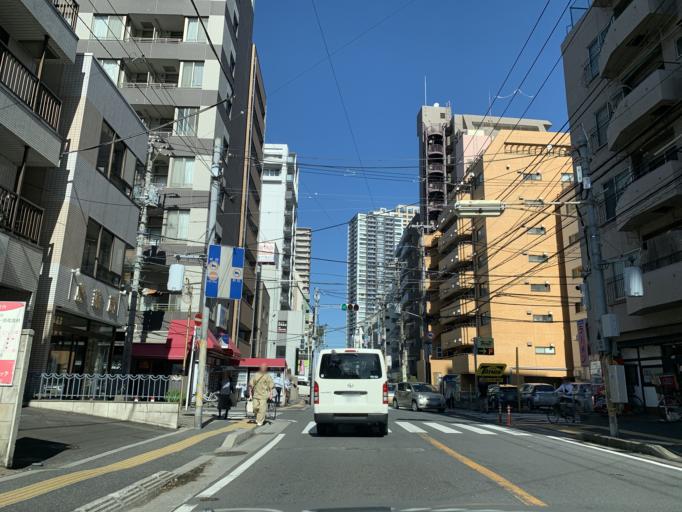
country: JP
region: Tokyo
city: Urayasu
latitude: 35.7199
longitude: 139.9245
